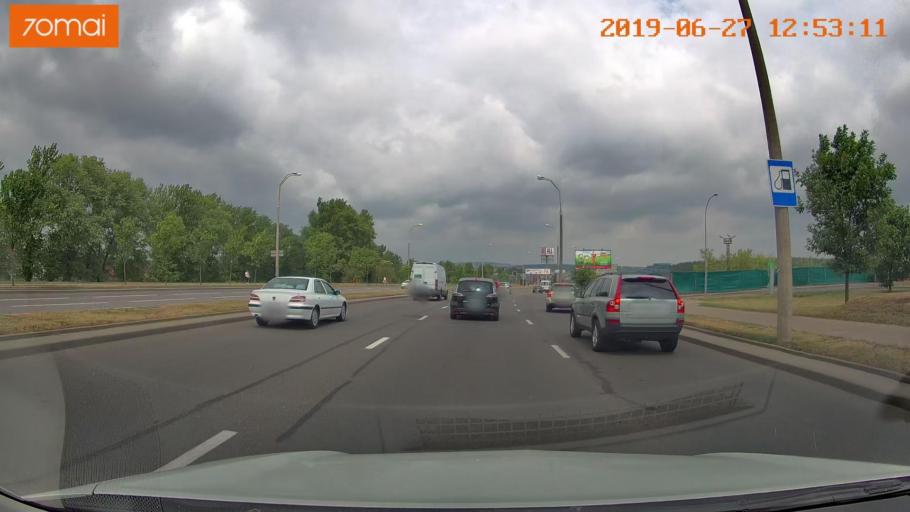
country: BY
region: Minsk
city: Bal'shavik
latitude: 53.9604
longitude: 27.5365
